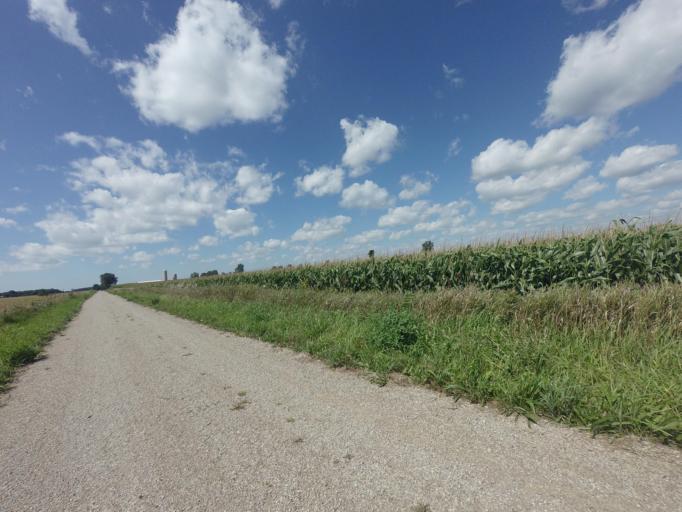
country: CA
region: Ontario
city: Huron East
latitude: 43.6626
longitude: -81.2568
